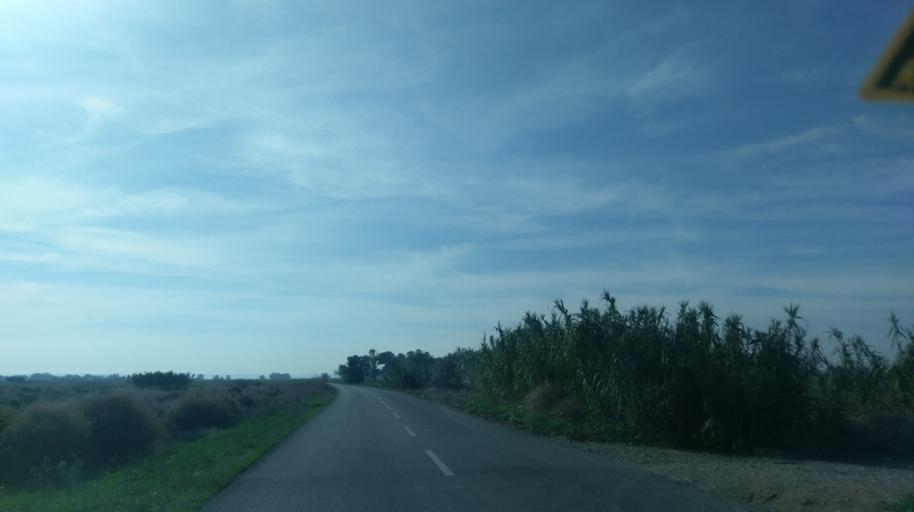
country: CY
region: Larnaka
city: Athienou
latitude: 35.1774
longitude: 33.5940
